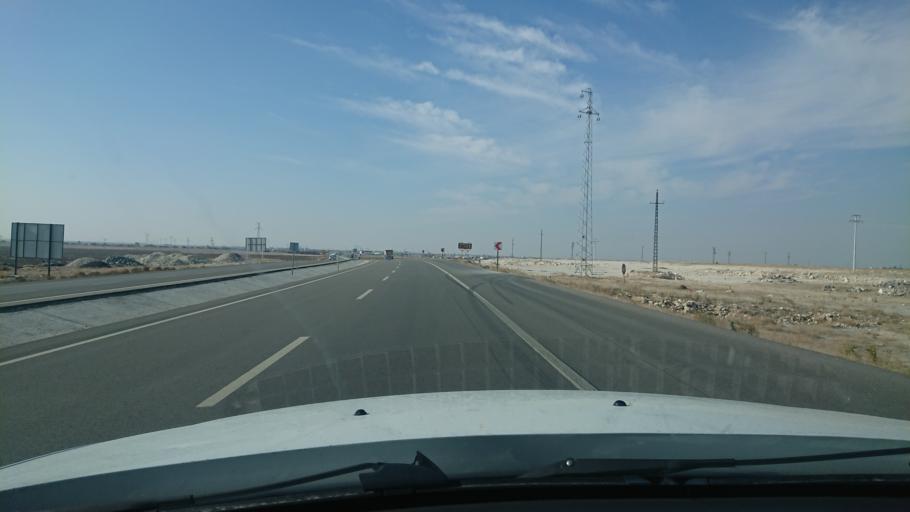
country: TR
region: Aksaray
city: Sultanhani
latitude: 38.2532
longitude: 33.4969
